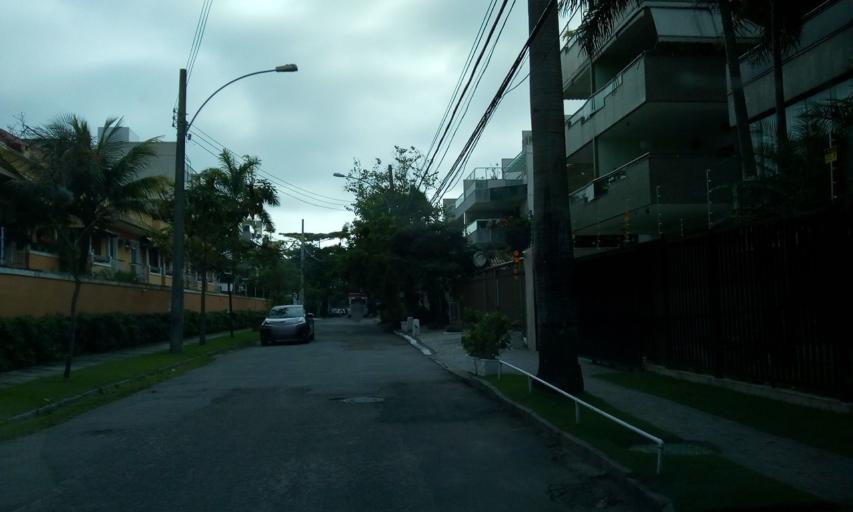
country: BR
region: Rio de Janeiro
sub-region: Nilopolis
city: Nilopolis
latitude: -23.0135
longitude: -43.4500
